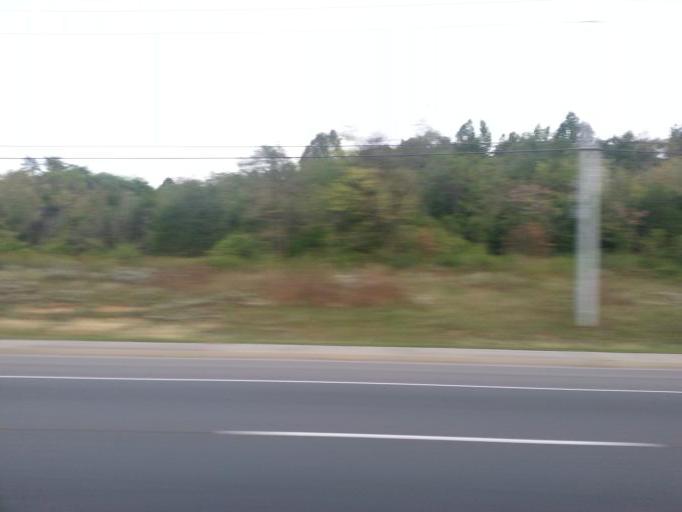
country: US
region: Tennessee
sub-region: Sevier County
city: Sevierville
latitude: 35.9103
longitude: -83.5813
